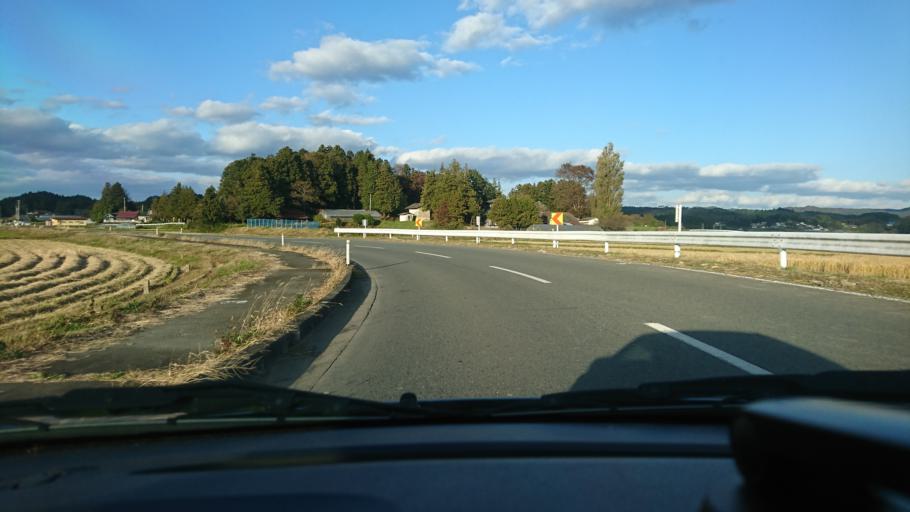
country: JP
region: Iwate
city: Ichinoseki
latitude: 38.7564
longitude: 141.2355
